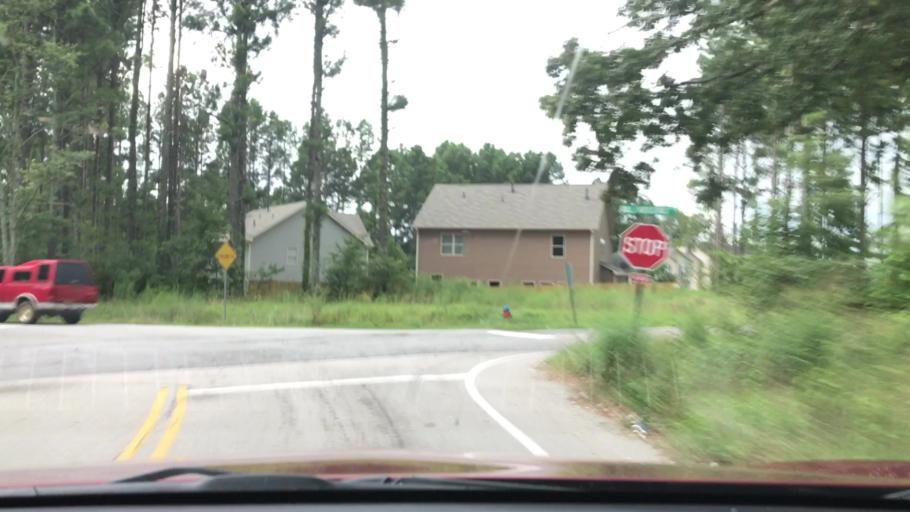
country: US
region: Georgia
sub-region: Barrow County
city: Winder
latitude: 33.9877
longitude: -83.7366
